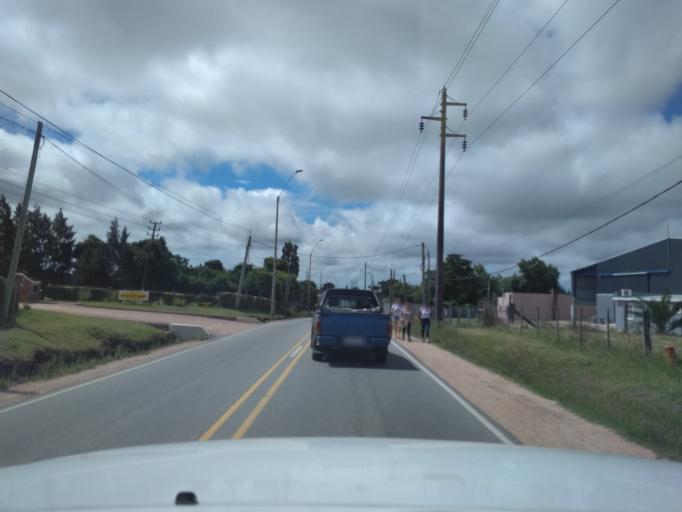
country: UY
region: Canelones
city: Pando
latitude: -34.7043
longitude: -55.9657
